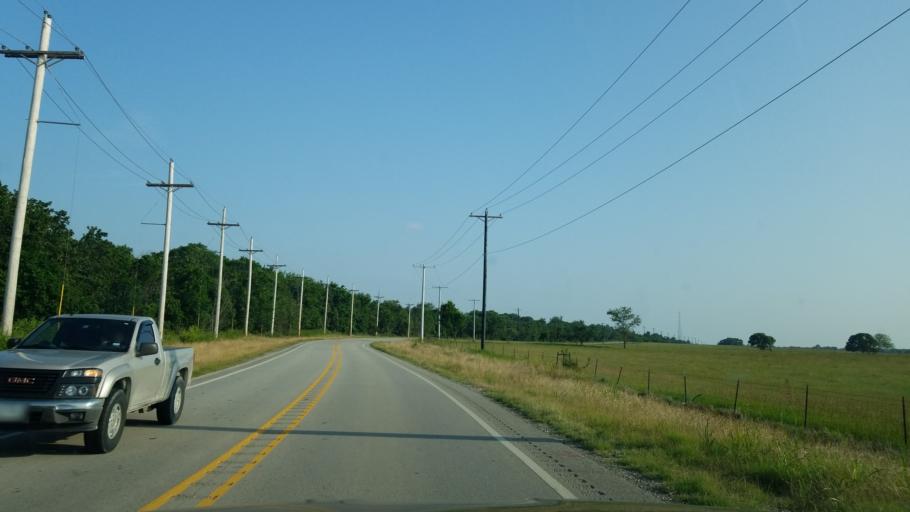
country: US
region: Texas
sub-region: Denton County
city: Aubrey
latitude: 33.3231
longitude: -96.9742
